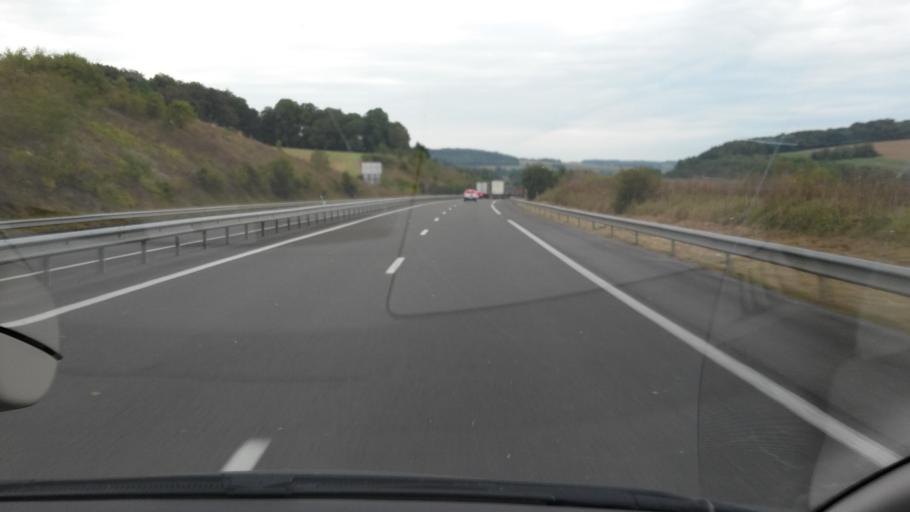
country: FR
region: Champagne-Ardenne
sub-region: Departement des Ardennes
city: La Francheville
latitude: 49.6588
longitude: 4.6357
